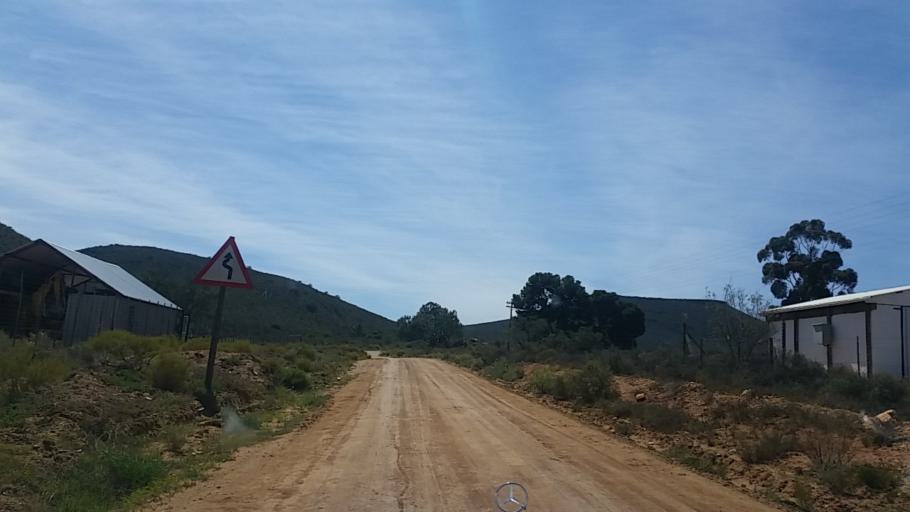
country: ZA
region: Western Cape
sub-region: Eden District Municipality
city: Knysna
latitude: -33.6421
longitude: 23.1409
